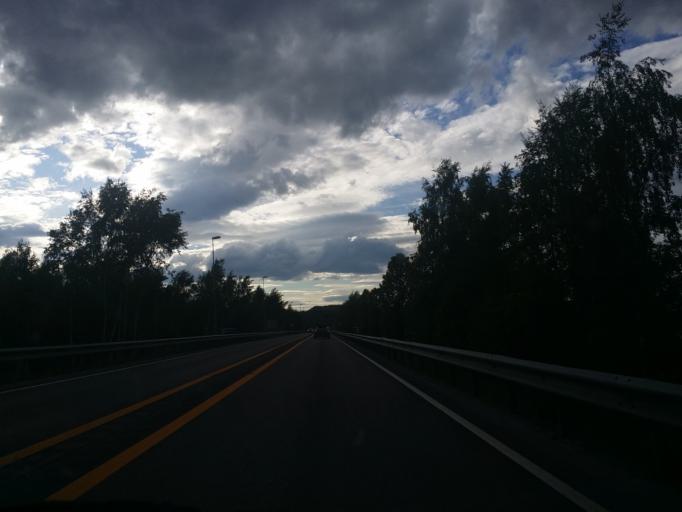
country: NO
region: Hedmark
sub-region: Ringsaker
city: Brumunddal
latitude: 60.8759
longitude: 10.9378
